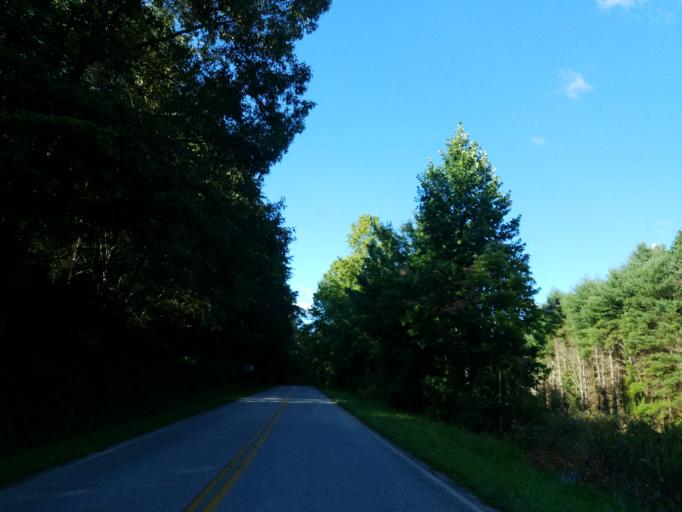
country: US
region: Georgia
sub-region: Fannin County
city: Blue Ridge
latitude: 34.7348
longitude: -84.2310
